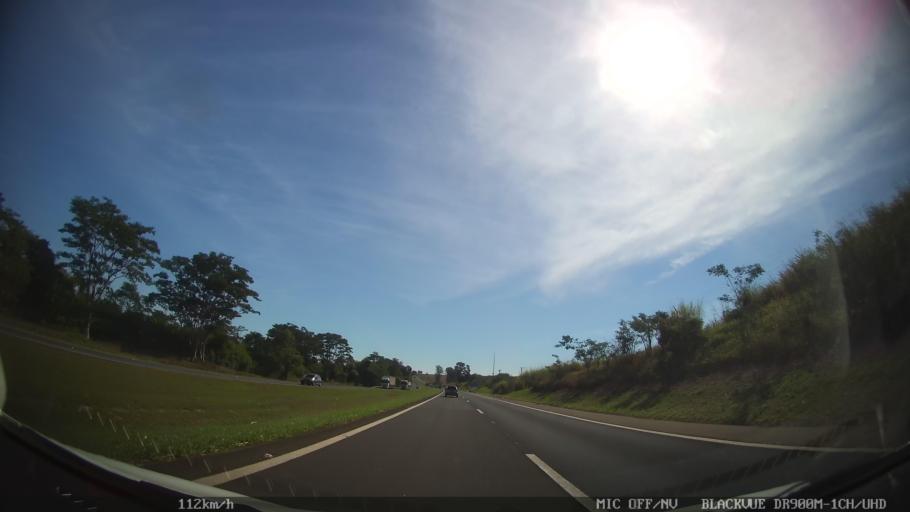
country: BR
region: Sao Paulo
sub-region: Porto Ferreira
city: Porto Ferreira
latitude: -21.8171
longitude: -47.4969
